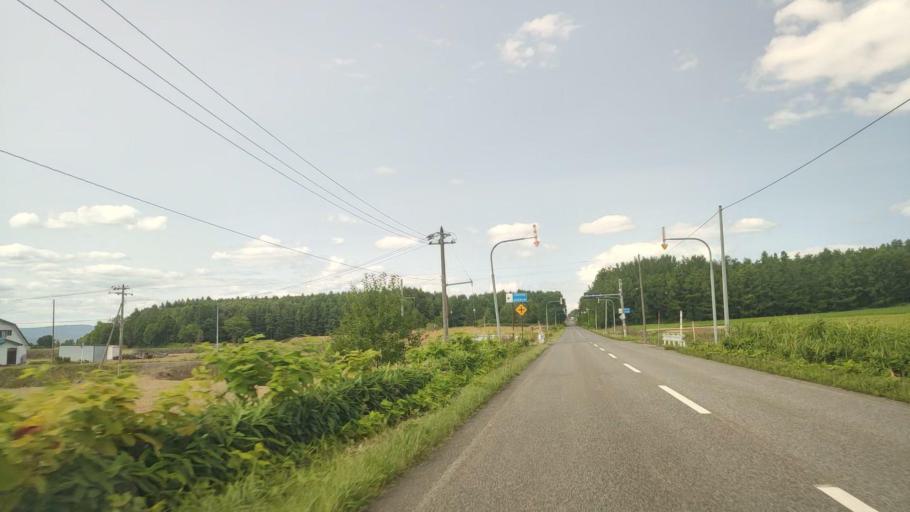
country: JP
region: Hokkaido
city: Nayoro
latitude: 44.2404
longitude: 142.4157
